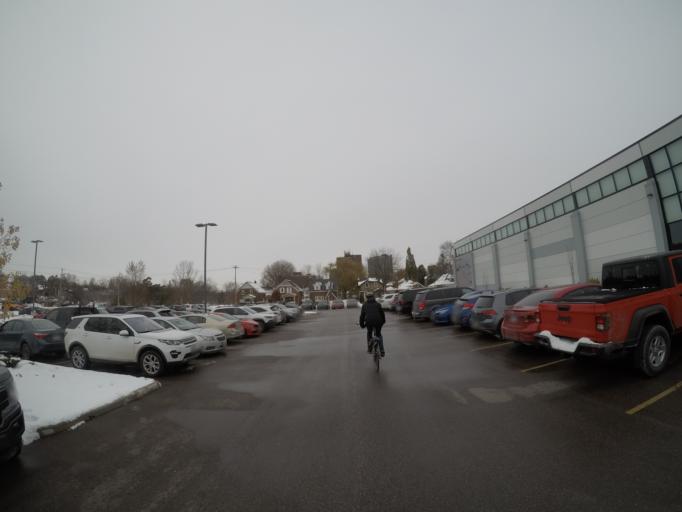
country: CA
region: Ontario
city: Waterloo
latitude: 43.4521
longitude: -80.5146
